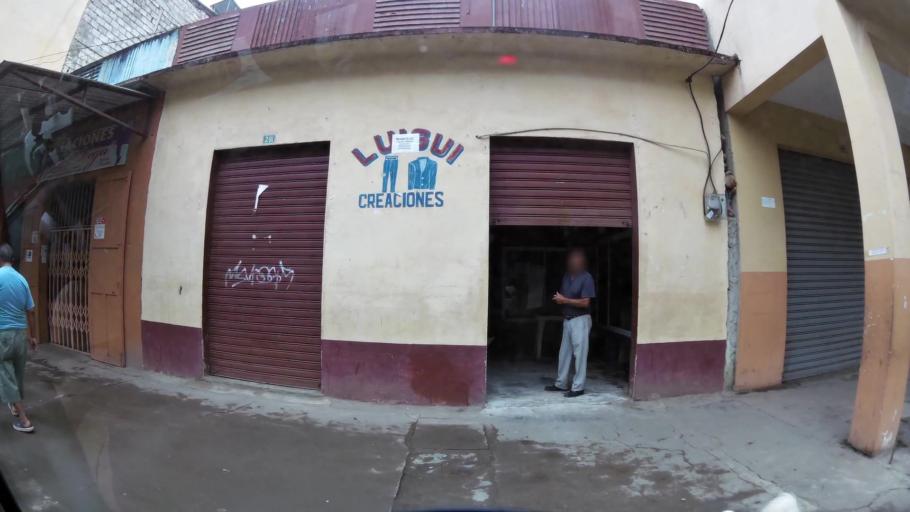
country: EC
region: El Oro
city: Pasaje
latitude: -3.3284
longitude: -79.8071
